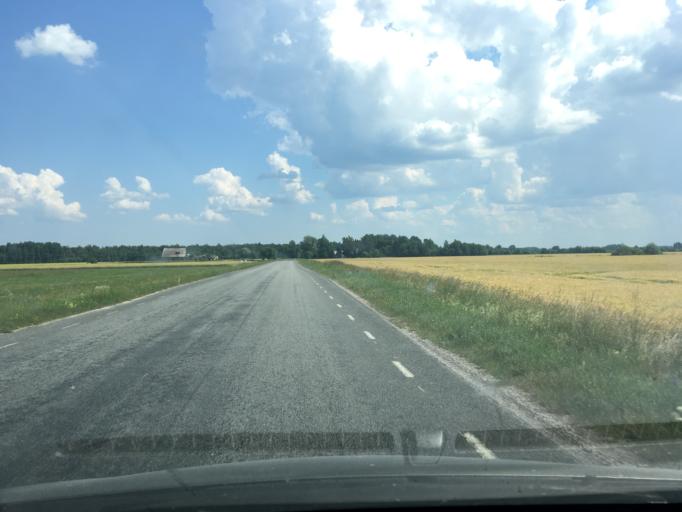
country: EE
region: Raplamaa
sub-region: Maerjamaa vald
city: Marjamaa
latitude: 58.7317
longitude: 24.2934
